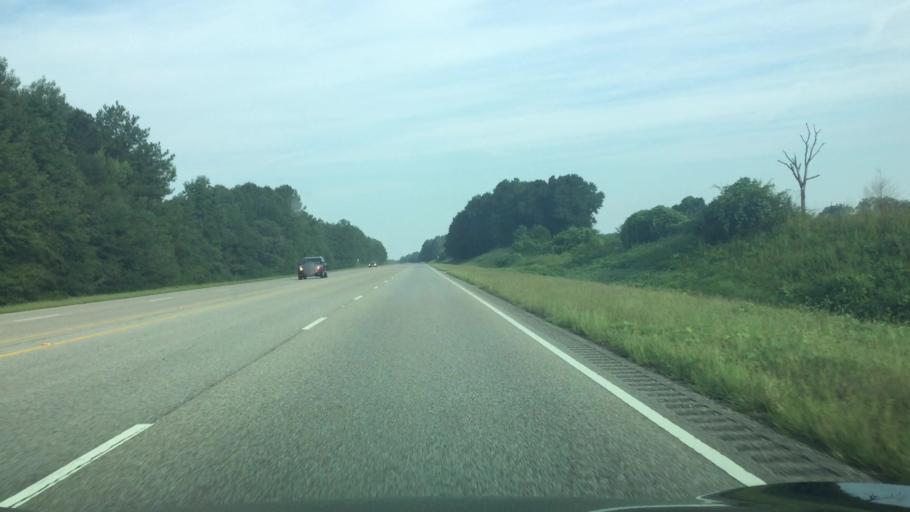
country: US
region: Alabama
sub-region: Covington County
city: Andalusia
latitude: 31.3997
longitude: -86.5820
